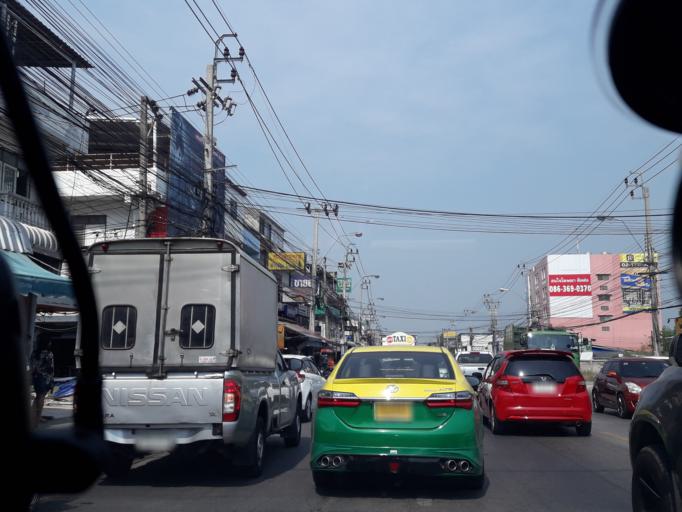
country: TH
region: Bangkok
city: Min Buri
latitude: 13.8231
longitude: 100.7205
